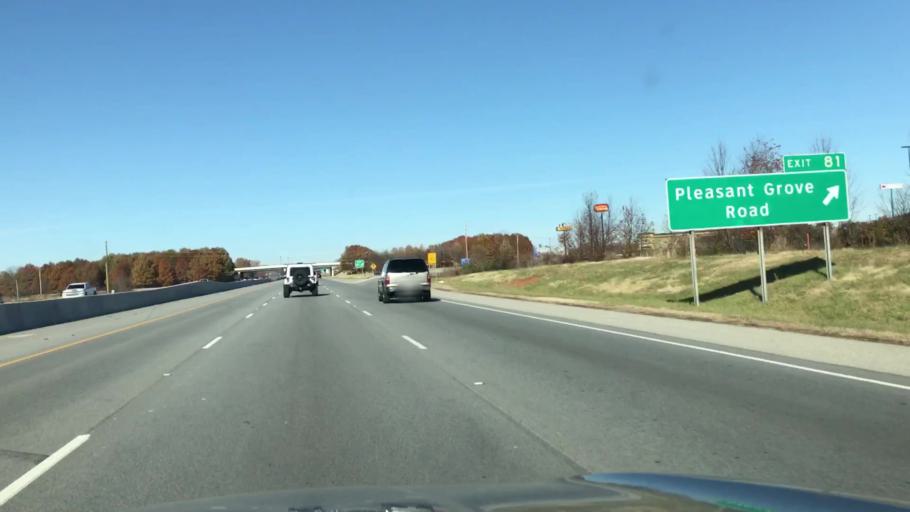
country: US
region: Arkansas
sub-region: Benton County
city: Lowell
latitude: 36.2796
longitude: -94.1537
